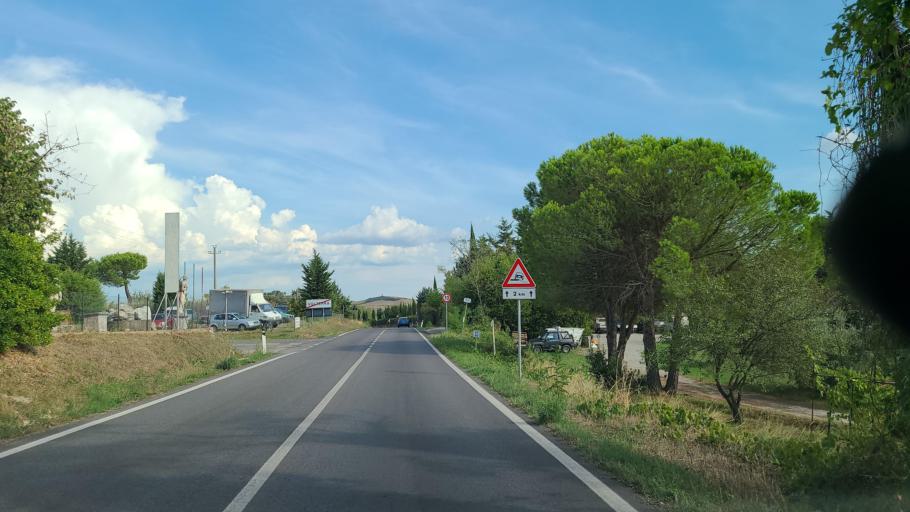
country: IT
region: Tuscany
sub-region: Province of Pisa
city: Volterra
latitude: 43.3968
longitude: 10.8849
